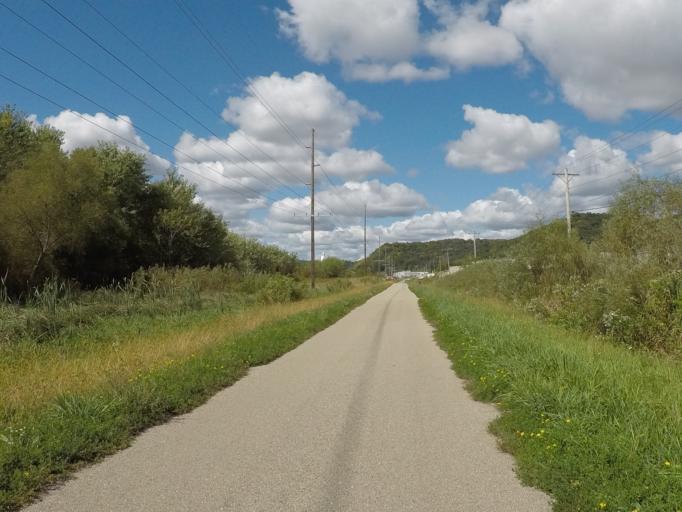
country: US
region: Wisconsin
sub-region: Richland County
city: Richland Center
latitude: 43.3158
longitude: -90.3592
